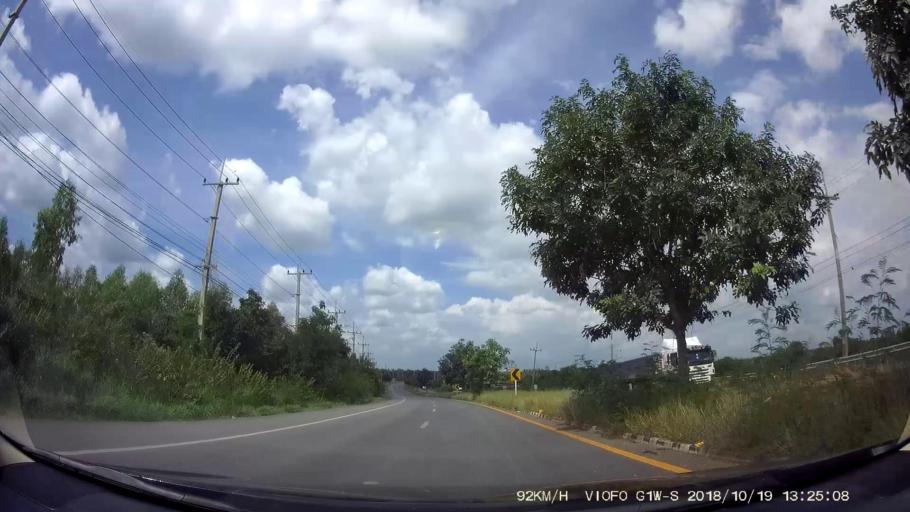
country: TH
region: Chaiyaphum
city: Chatturat
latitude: 15.5169
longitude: 101.8250
